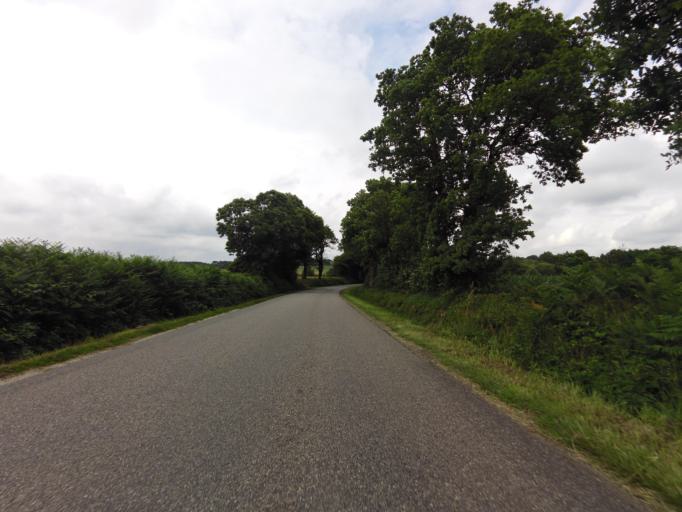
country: FR
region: Brittany
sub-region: Departement du Morbihan
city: Limerzel
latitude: 47.6232
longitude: -2.4022
